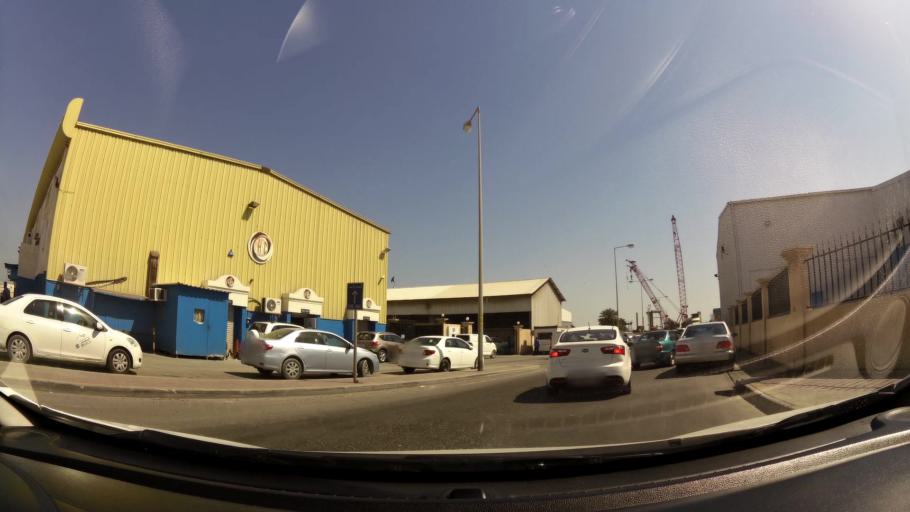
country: BH
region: Manama
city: Manama
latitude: 26.2003
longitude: 50.6021
